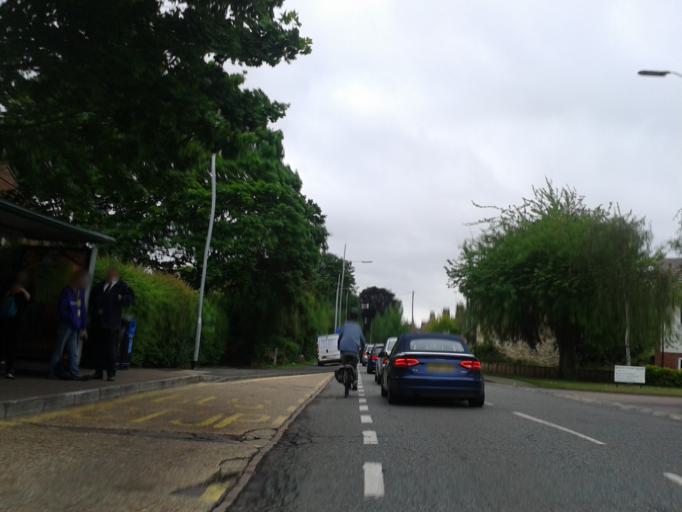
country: GB
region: England
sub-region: Cambridgeshire
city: Histon
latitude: 52.2279
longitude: 0.1119
